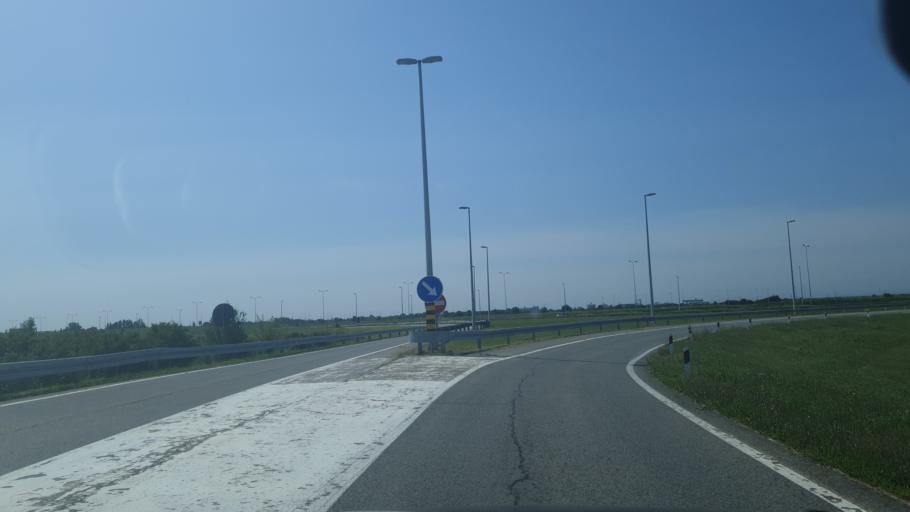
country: RS
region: Autonomna Pokrajina Vojvodina
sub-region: Sremski Okrug
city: Pecinci
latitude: 44.9245
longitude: 19.9540
